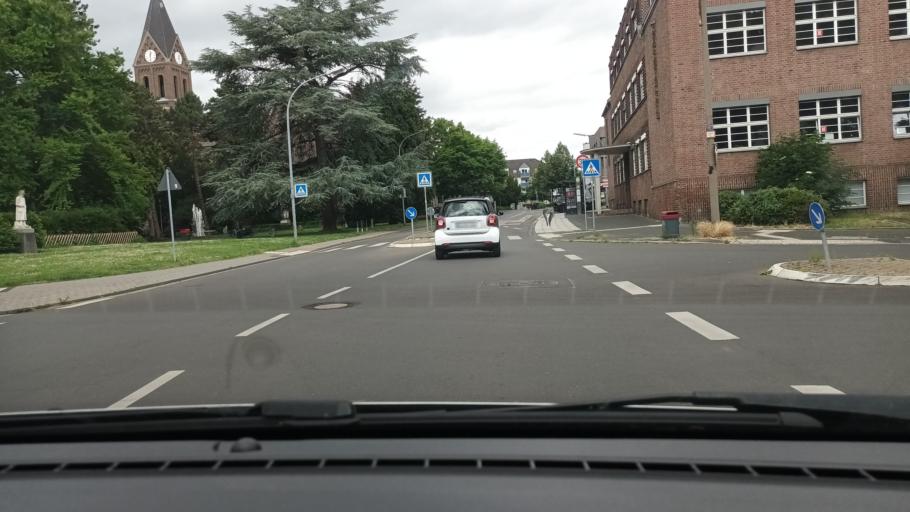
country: DE
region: North Rhine-Westphalia
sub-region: Regierungsbezirk Koln
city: Hurth
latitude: 50.8701
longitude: 6.8693
